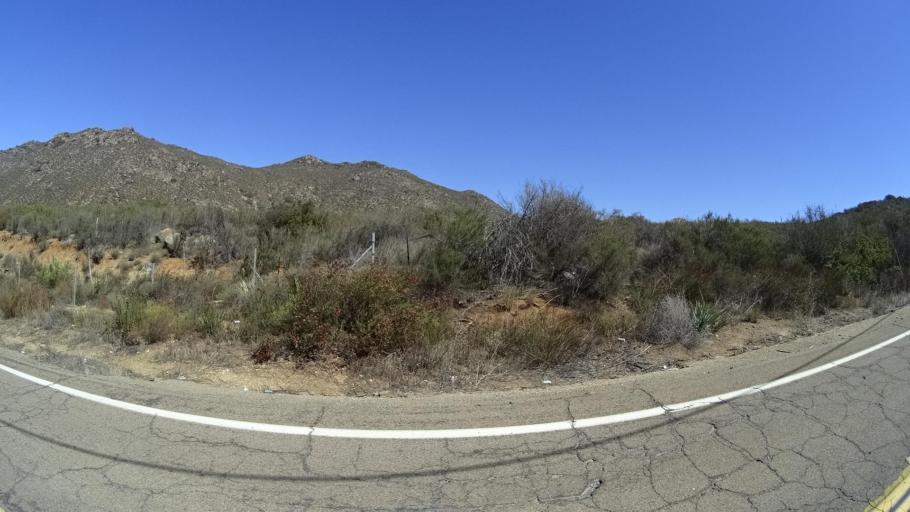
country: US
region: California
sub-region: San Diego County
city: Alpine
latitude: 32.7924
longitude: -116.7400
